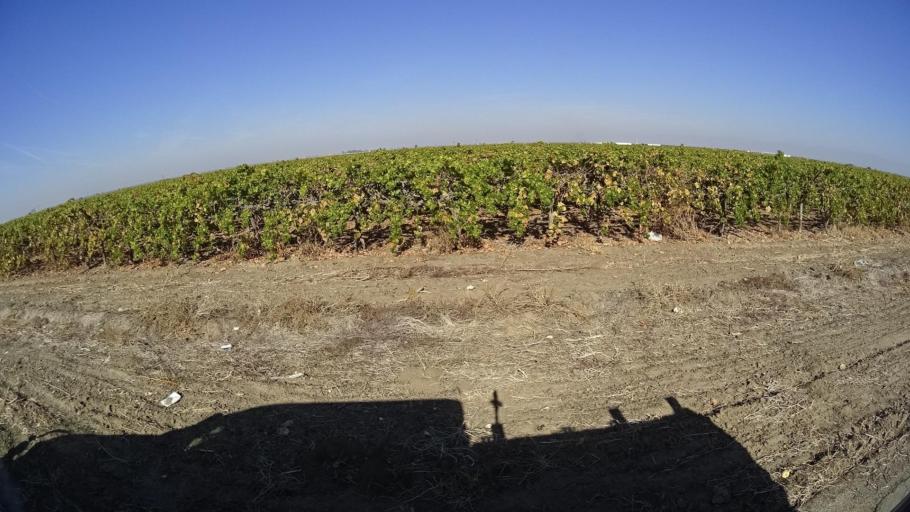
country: US
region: California
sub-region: Kern County
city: McFarland
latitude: 35.7035
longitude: -119.1646
